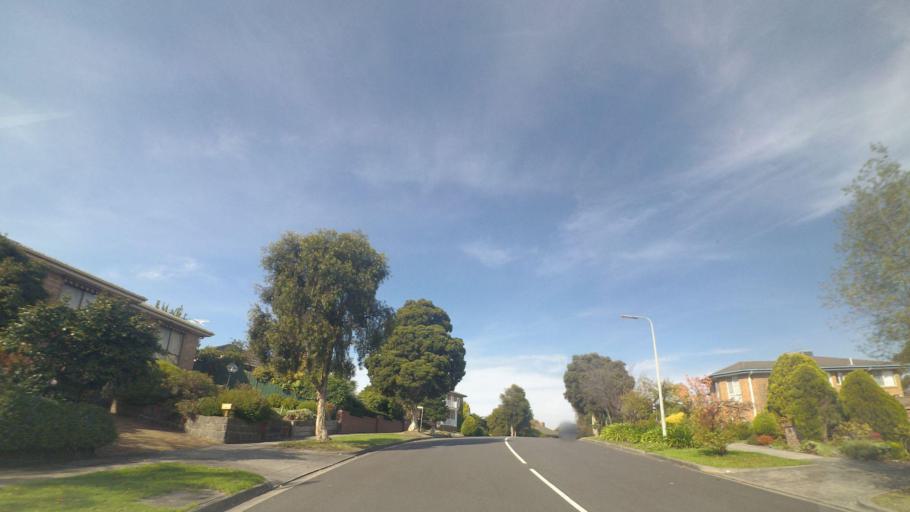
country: AU
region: Victoria
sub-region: Manningham
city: Doncaster East
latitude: -37.7693
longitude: 145.1489
